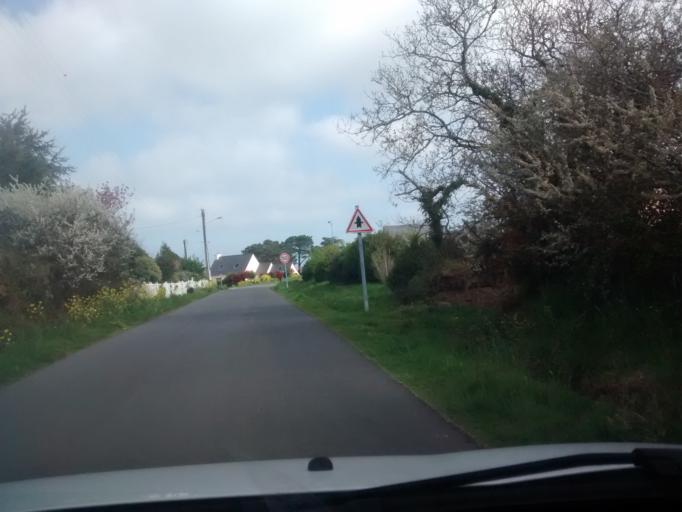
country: FR
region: Brittany
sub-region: Departement des Cotes-d'Armor
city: Penvenan
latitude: 48.8311
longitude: -3.3091
